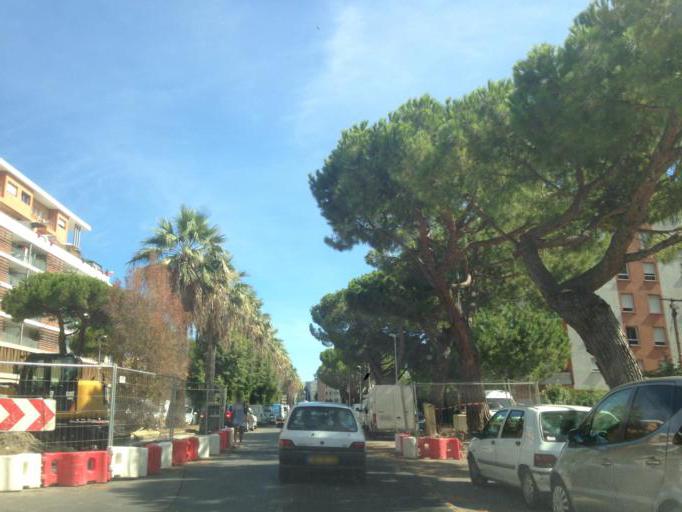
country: FR
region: Provence-Alpes-Cote d'Azur
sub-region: Departement des Alpes-Maritimes
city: Saint-Laurent-du-Var
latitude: 43.6734
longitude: 7.2086
